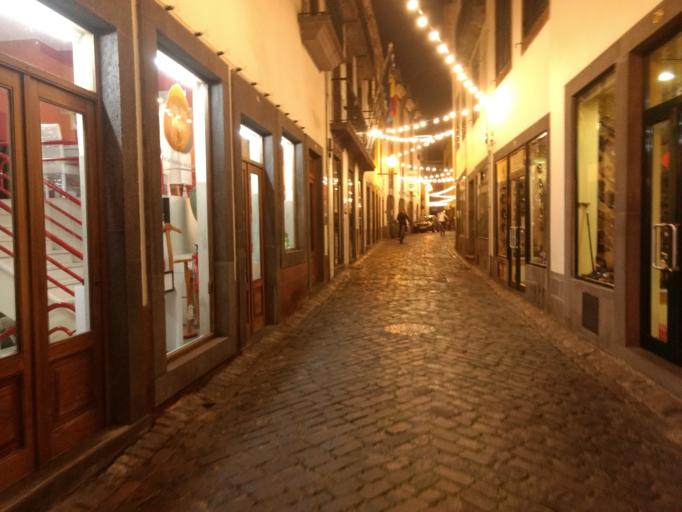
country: PT
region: Madeira
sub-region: Funchal
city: Funchal
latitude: 32.6477
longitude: -16.9073
